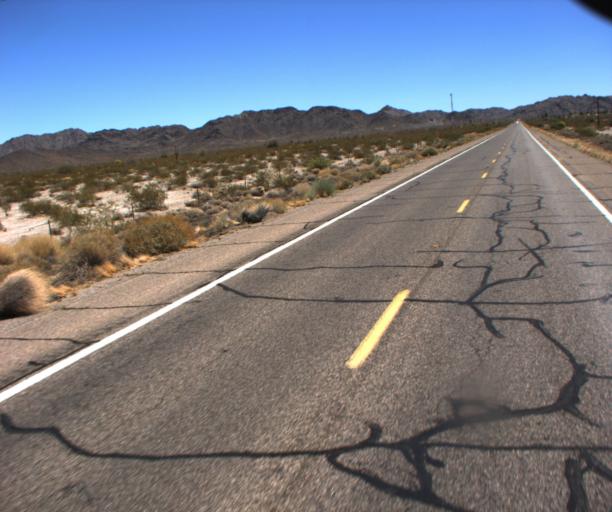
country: US
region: Arizona
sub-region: La Paz County
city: Salome
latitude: 33.7222
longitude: -113.7188
